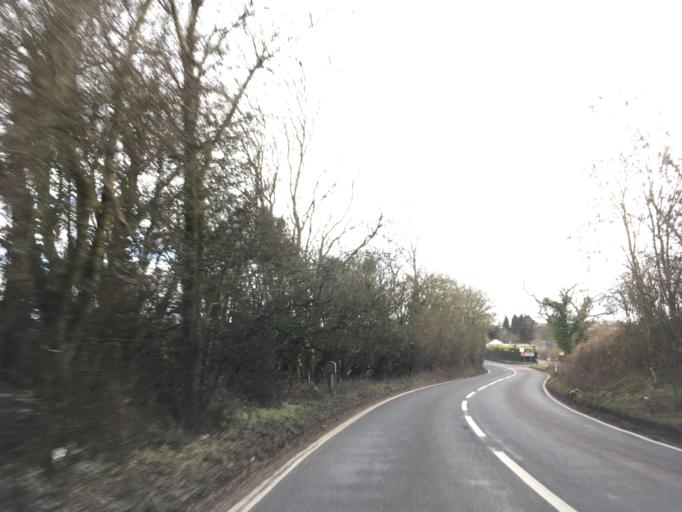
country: GB
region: England
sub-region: South Gloucestershire
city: Tytherington
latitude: 51.5626
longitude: -2.4910
